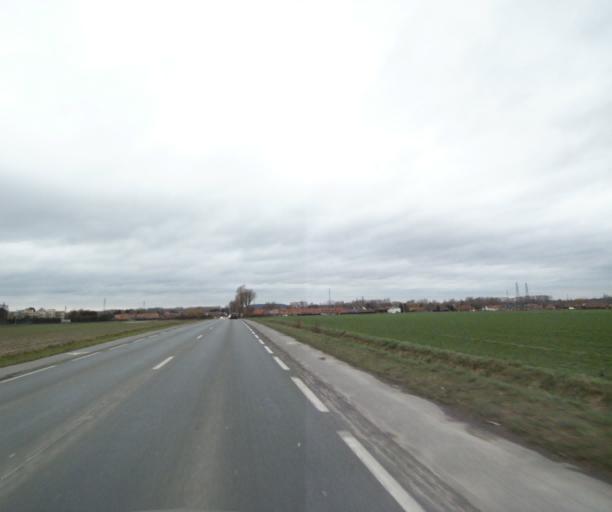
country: FR
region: Nord-Pas-de-Calais
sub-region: Departement du Nord
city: Saint-Saulve
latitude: 50.3781
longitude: 3.5645
